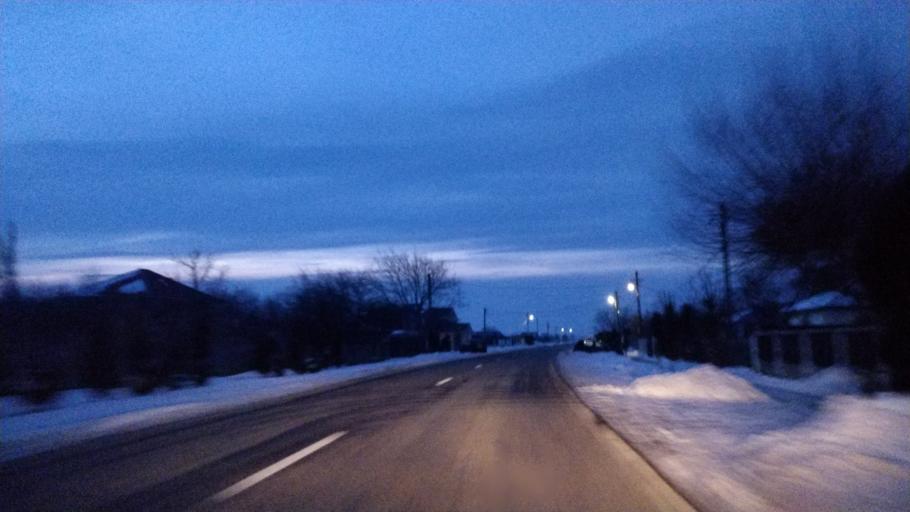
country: RO
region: Vrancea
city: Vulturu de Sus
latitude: 45.6376
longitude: 27.3732
